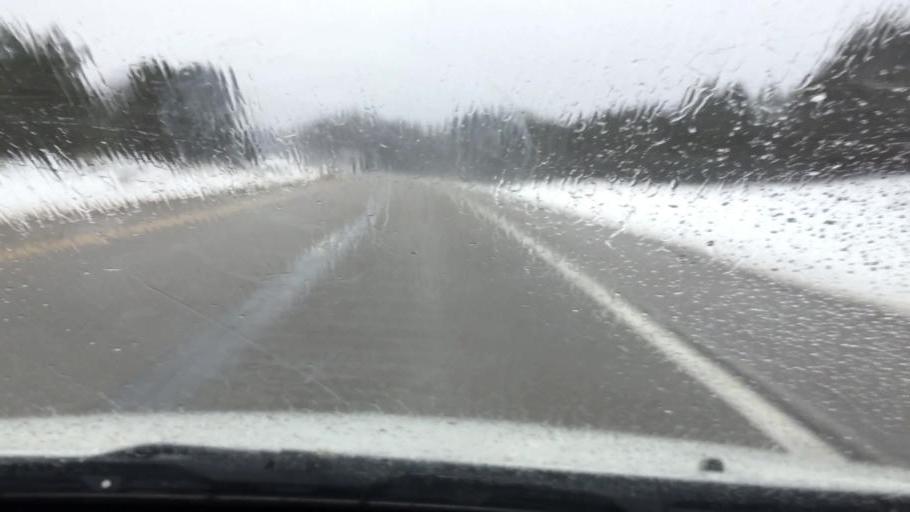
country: US
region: Michigan
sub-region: Wexford County
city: Cadillac
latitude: 44.1472
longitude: -85.4652
